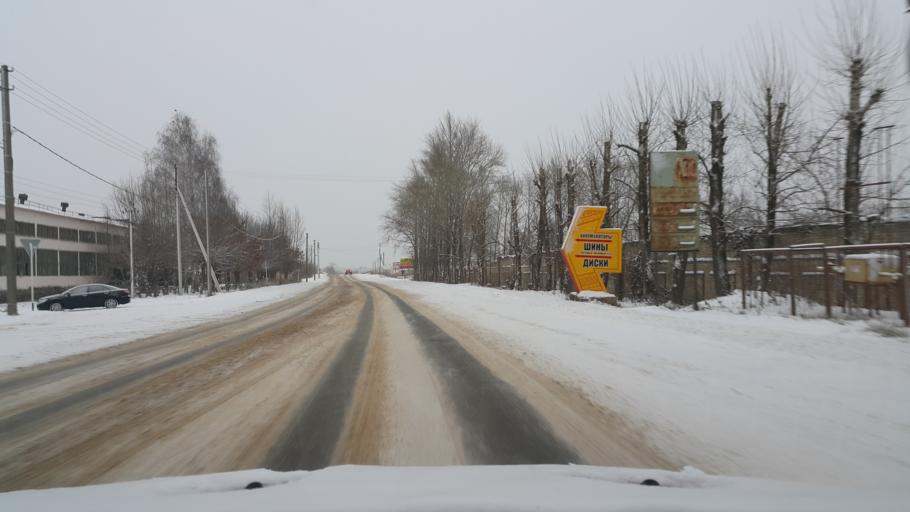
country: RU
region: Tambov
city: Pokrovo-Prigorodnoye
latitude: 52.6574
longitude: 41.4291
